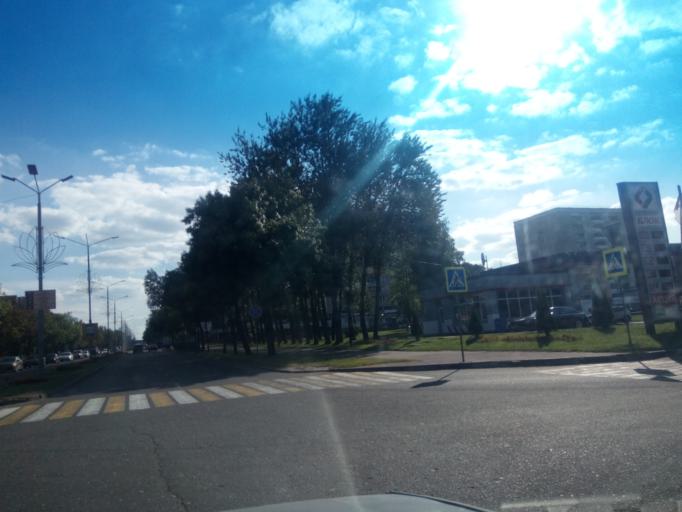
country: BY
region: Vitebsk
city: Navapolatsk
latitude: 55.5353
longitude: 28.6622
